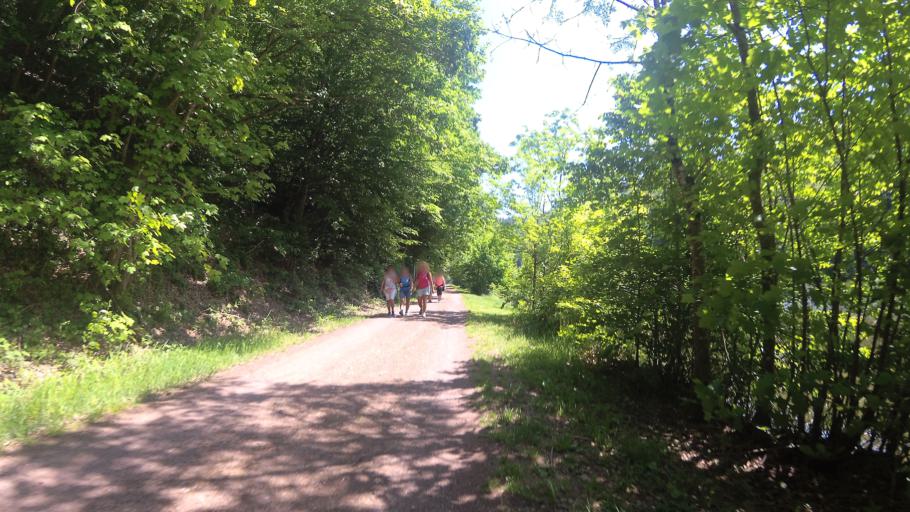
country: DE
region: Saarland
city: Mettlach
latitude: 49.4971
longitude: 6.5667
